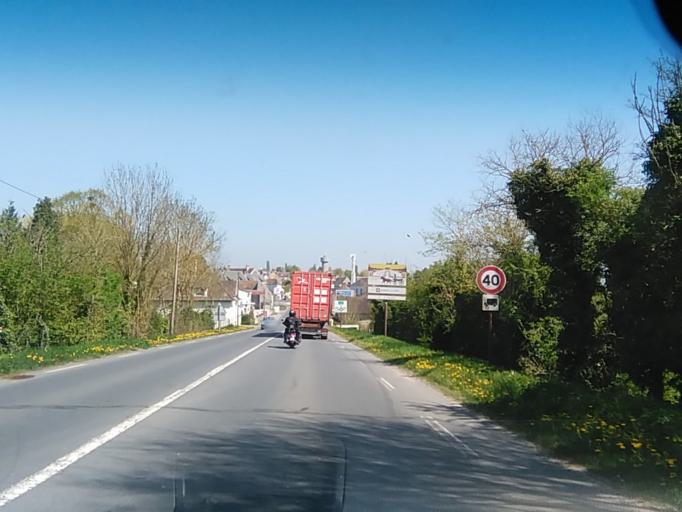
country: FR
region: Lower Normandy
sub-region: Departement de l'Orne
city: Sees
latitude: 48.7048
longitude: 0.2219
